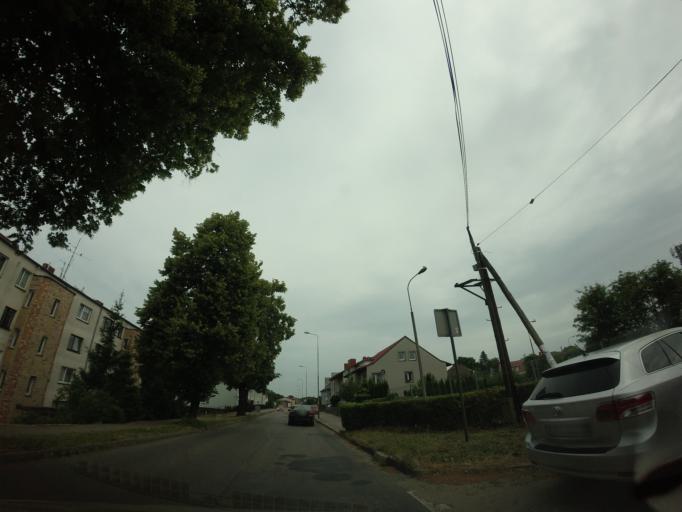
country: PL
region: West Pomeranian Voivodeship
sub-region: Powiat drawski
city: Czaplinek
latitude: 53.5539
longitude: 16.2326
